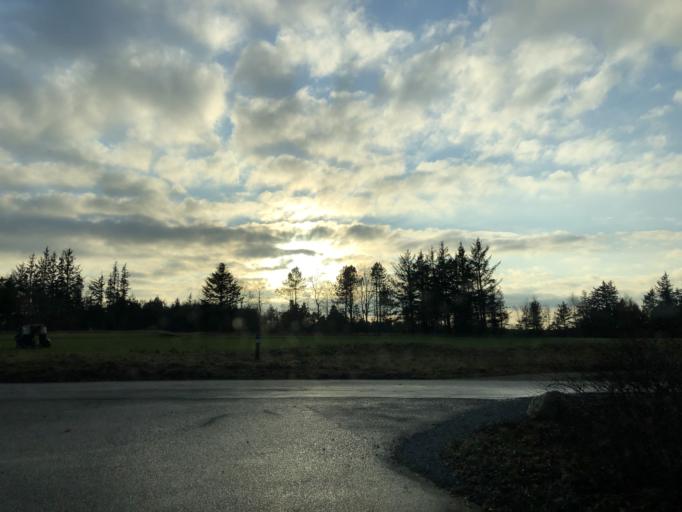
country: DK
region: Central Jutland
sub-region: Holstebro Kommune
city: Ulfborg
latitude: 56.3215
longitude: 8.4286
